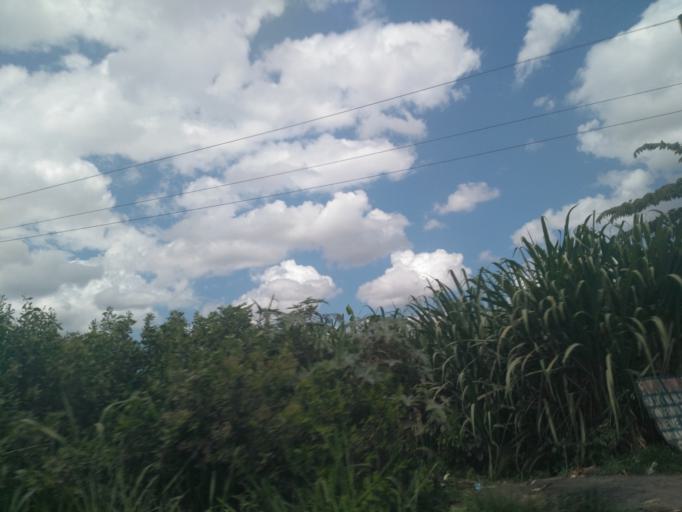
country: TZ
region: Dar es Salaam
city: Dar es Salaam
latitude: -6.9046
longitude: 39.2381
